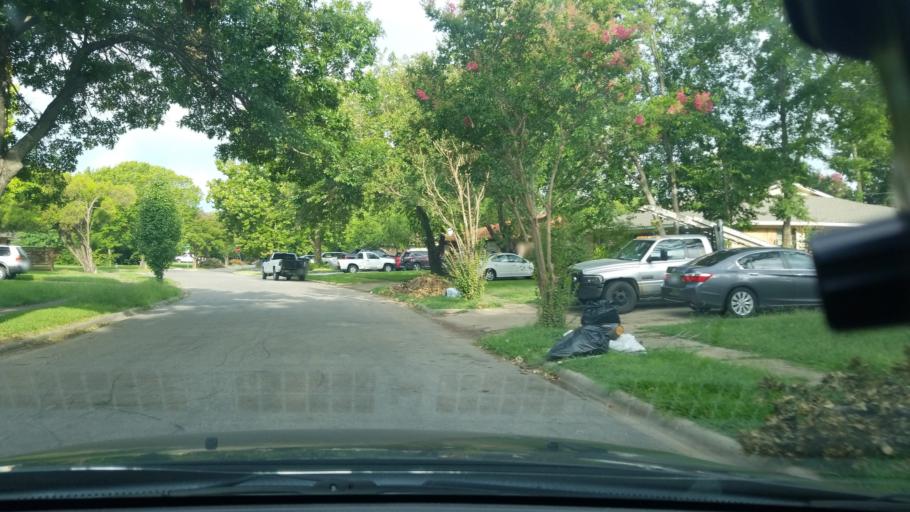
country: US
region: Texas
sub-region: Dallas County
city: Mesquite
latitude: 32.8261
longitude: -96.6626
